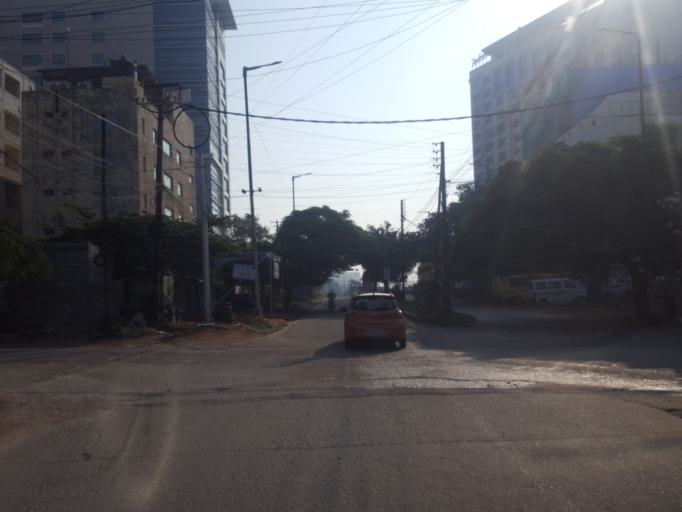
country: IN
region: Telangana
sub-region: Rangareddi
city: Kukatpalli
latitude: 17.4482
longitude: 78.3617
